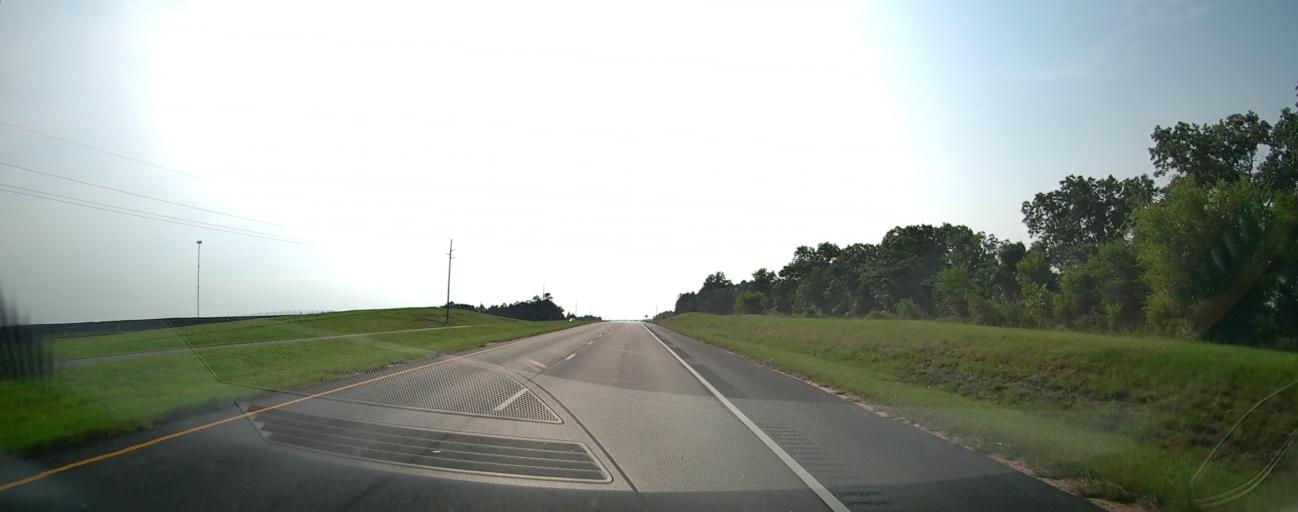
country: US
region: Georgia
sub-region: Taylor County
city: Butler
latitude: 32.5789
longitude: -84.3162
